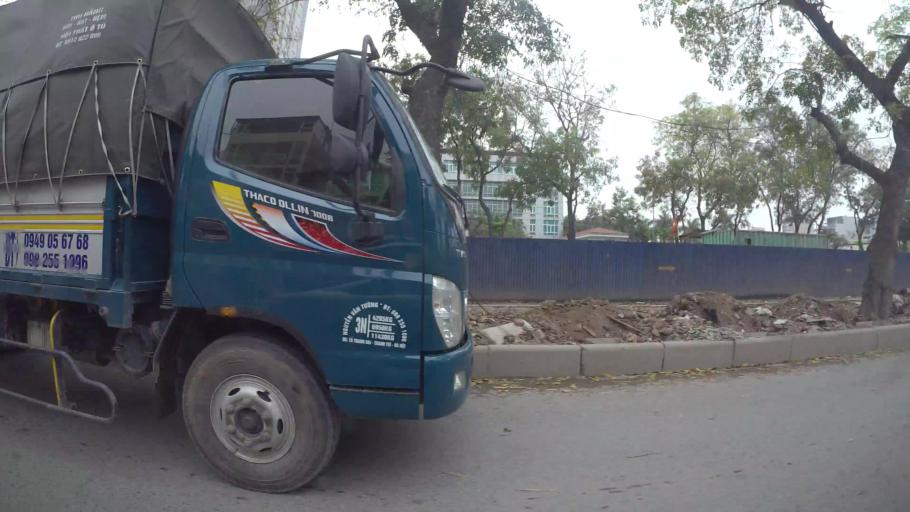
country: VN
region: Ha Noi
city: Cau Dien
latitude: 21.0430
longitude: 105.7809
